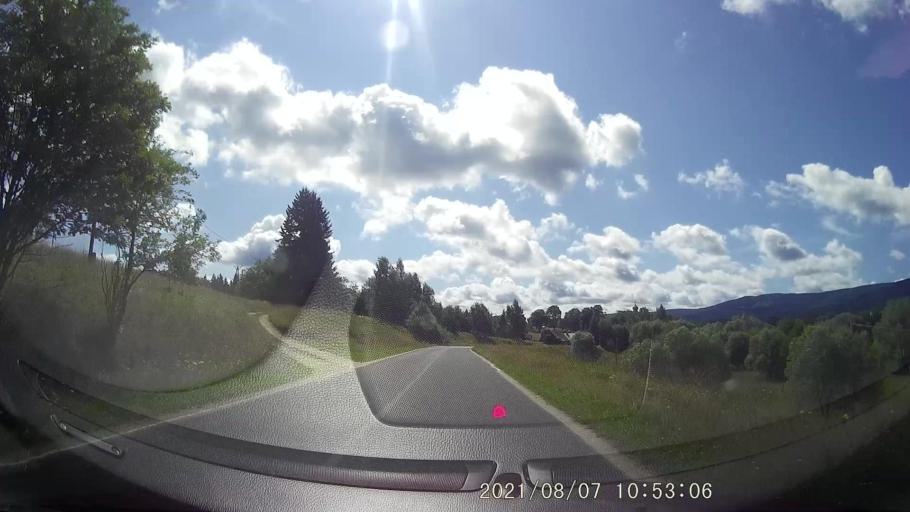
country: CZ
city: Rokytnice v Orlickych Horach
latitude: 50.2780
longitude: 16.4800
